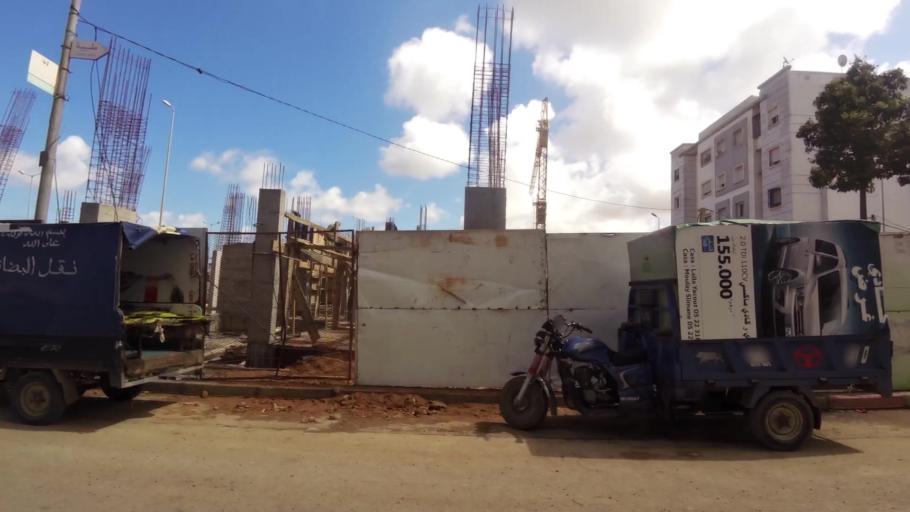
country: MA
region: Grand Casablanca
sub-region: Nouaceur
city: Dar Bouazza
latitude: 33.5355
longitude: -7.7216
